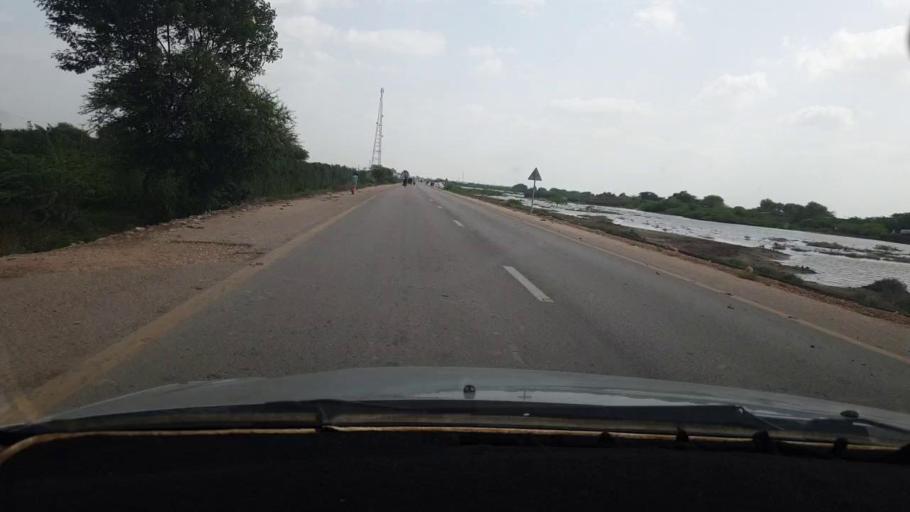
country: PK
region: Sindh
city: Naukot
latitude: 24.9948
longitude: 69.2907
